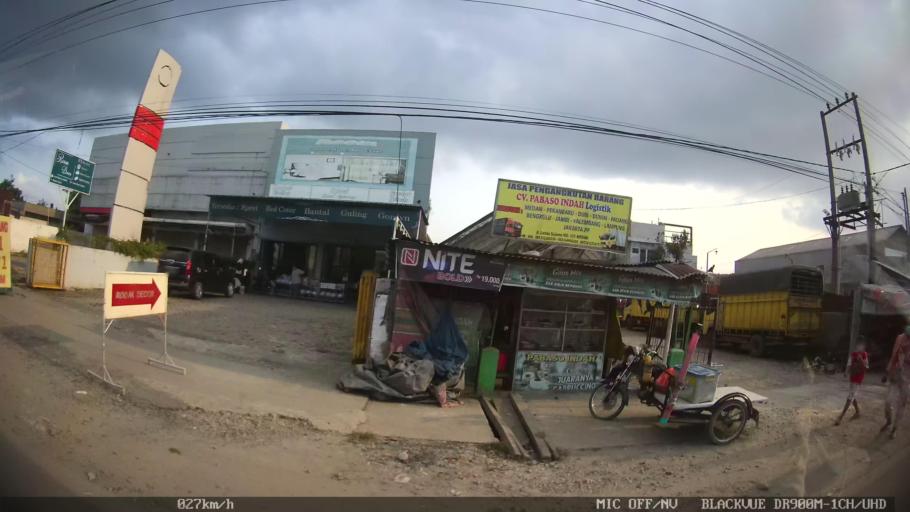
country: ID
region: North Sumatra
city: Medan
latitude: 3.5970
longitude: 98.7344
